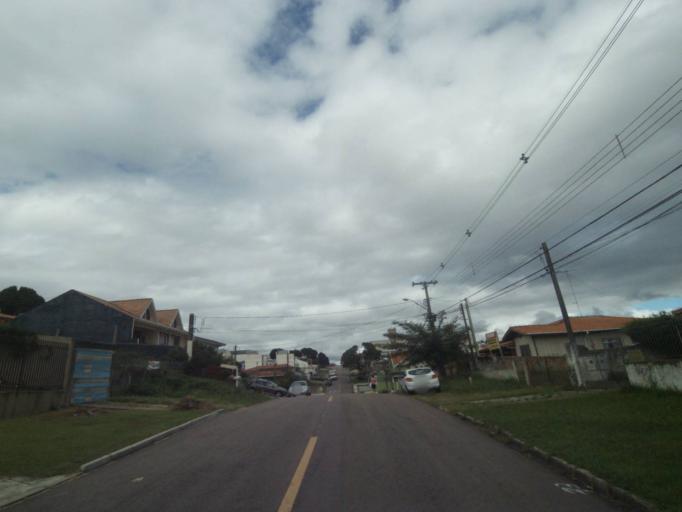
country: BR
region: Parana
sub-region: Curitiba
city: Curitiba
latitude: -25.4774
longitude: -49.2786
